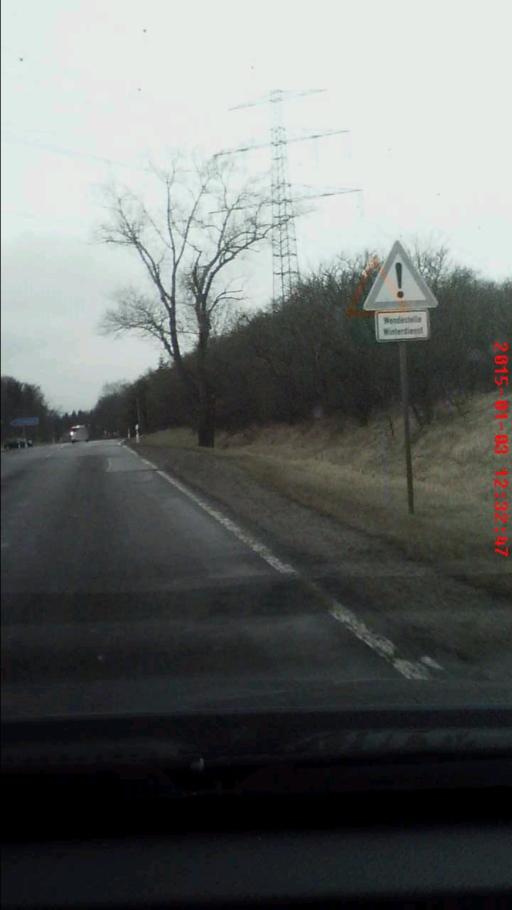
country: DE
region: Thuringia
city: Klettbach
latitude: 50.9237
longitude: 11.1422
